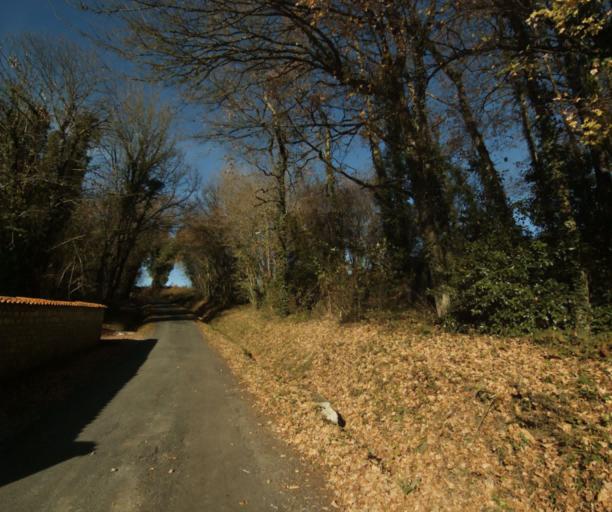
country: FR
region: Poitou-Charentes
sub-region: Departement de la Charente-Maritime
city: Chaniers
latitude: 45.7550
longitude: -0.5093
